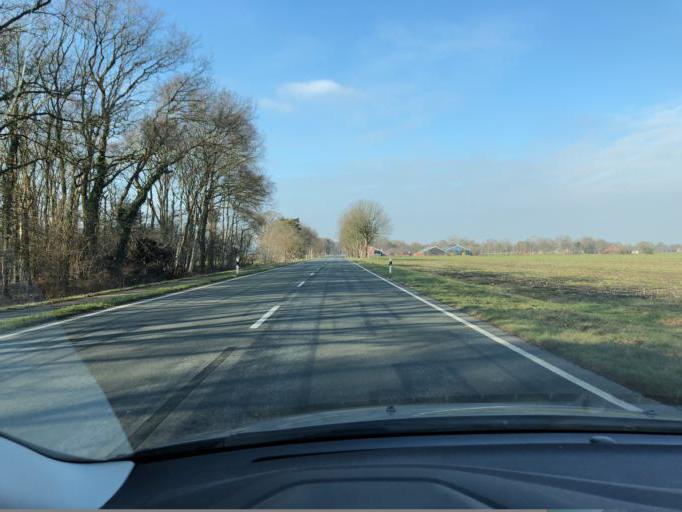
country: DE
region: Lower Saxony
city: Schwerinsdorf
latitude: 53.2951
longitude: 7.6887
